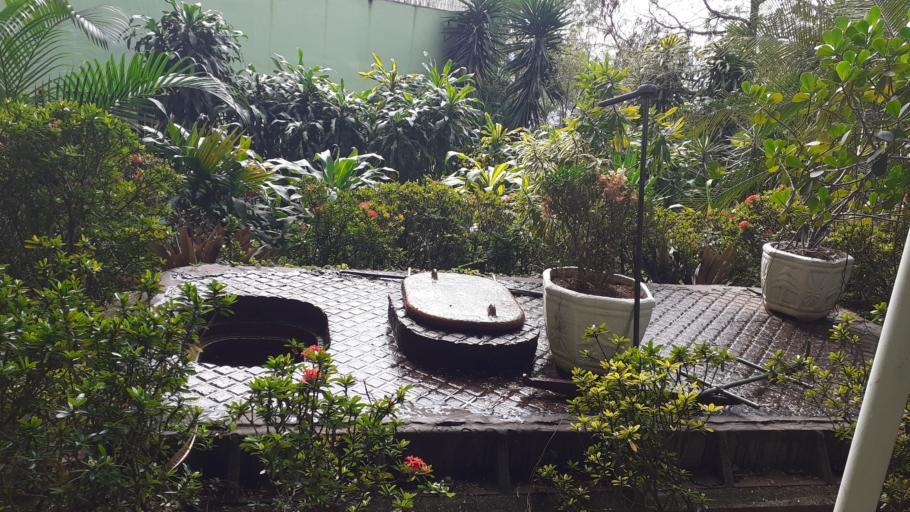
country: BR
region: Rio de Janeiro
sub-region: Nova Iguacu
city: Nova Iguacu
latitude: -22.7637
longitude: -43.4518
